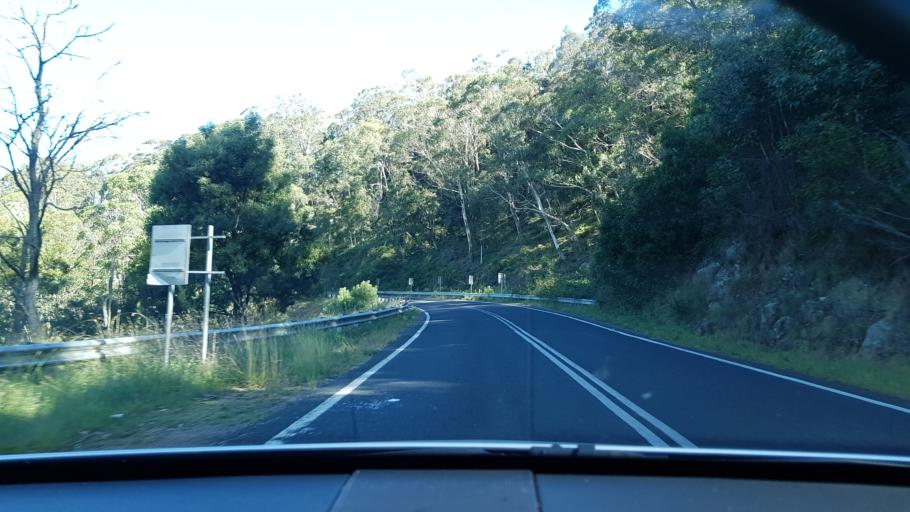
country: AU
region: New South Wales
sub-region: Lithgow
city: Bowenfels
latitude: -33.6660
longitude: 150.0489
